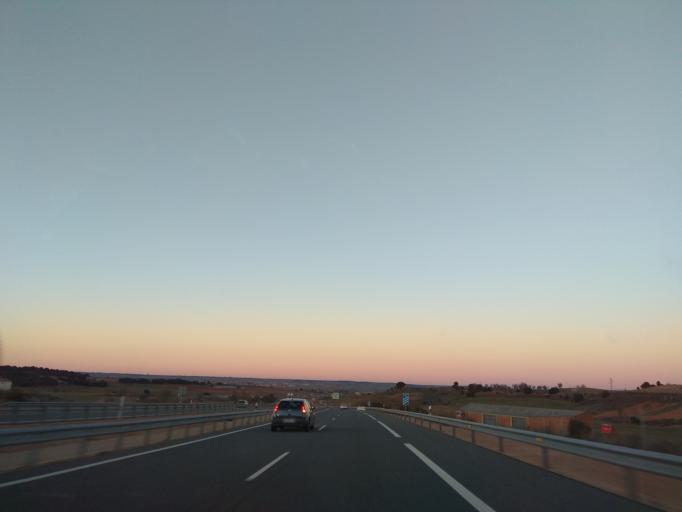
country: ES
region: Castille and Leon
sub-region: Provincia de Burgos
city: Quintanilla de la Mata
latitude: 41.9887
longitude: -3.7635
